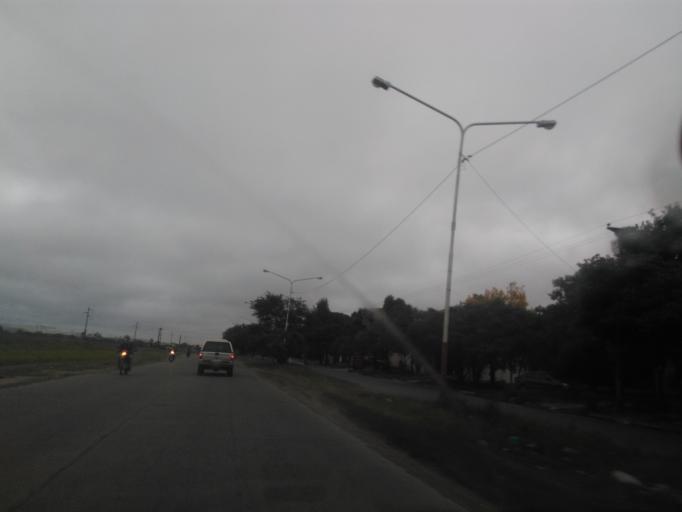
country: AR
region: Chaco
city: Resistencia
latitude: -27.4594
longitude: -59.0204
